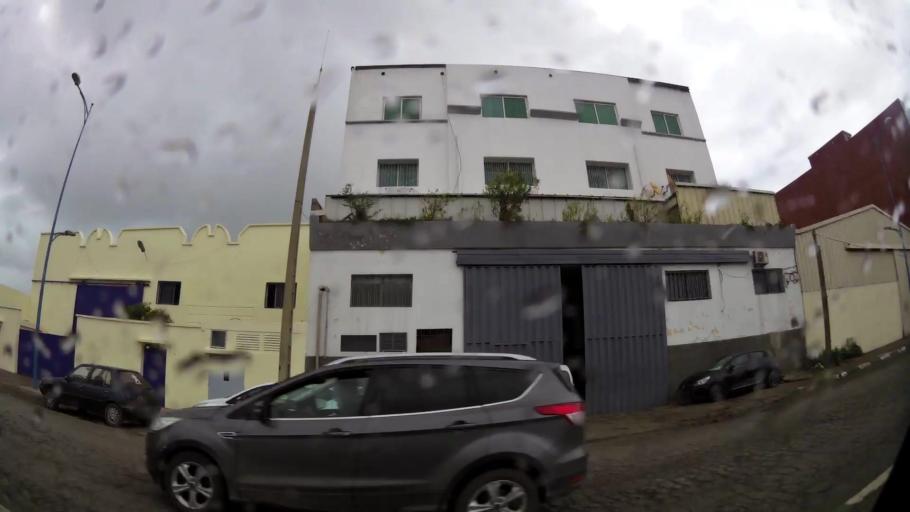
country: MA
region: Grand Casablanca
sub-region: Mediouna
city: Tit Mellil
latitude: 33.6228
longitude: -7.5044
